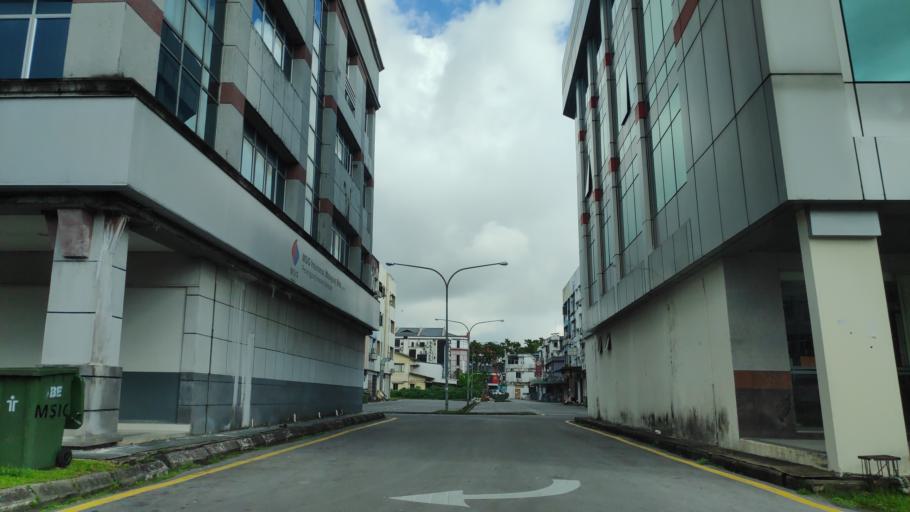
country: MY
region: Sarawak
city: Kuching
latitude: 1.5514
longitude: 110.3341
